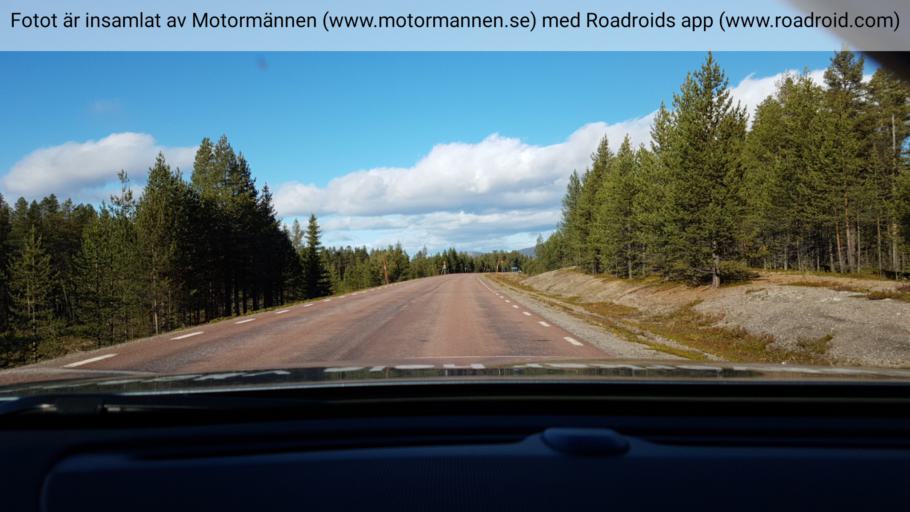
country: SE
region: Norrbotten
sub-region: Arjeplogs Kommun
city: Arjeplog
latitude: 66.0385
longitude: 18.0437
